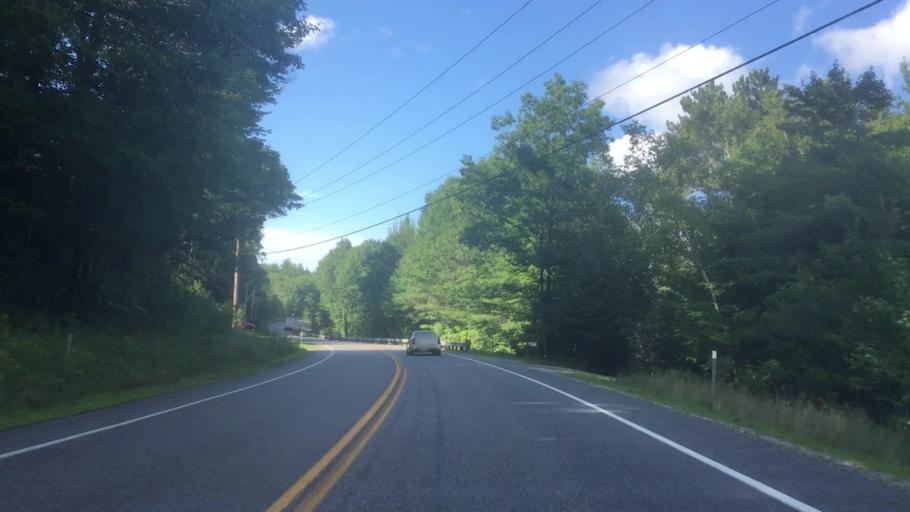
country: US
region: New Hampshire
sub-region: Hillsborough County
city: Hillsborough
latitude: 43.1048
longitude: -71.9566
